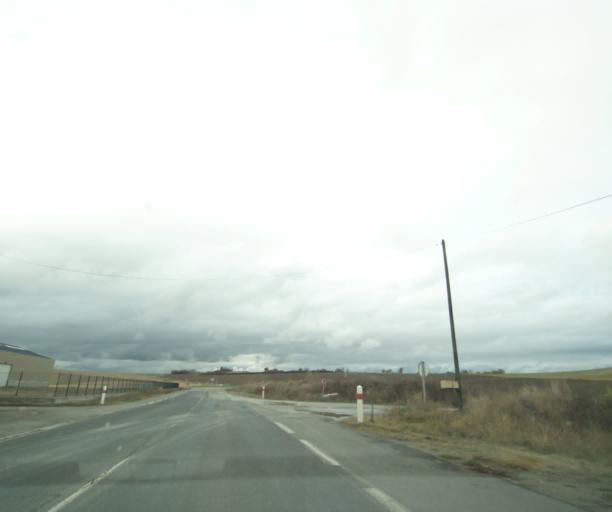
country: FR
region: Auvergne
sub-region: Departement du Puy-de-Dome
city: Pont-du-Chateau
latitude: 45.8170
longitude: 3.2591
